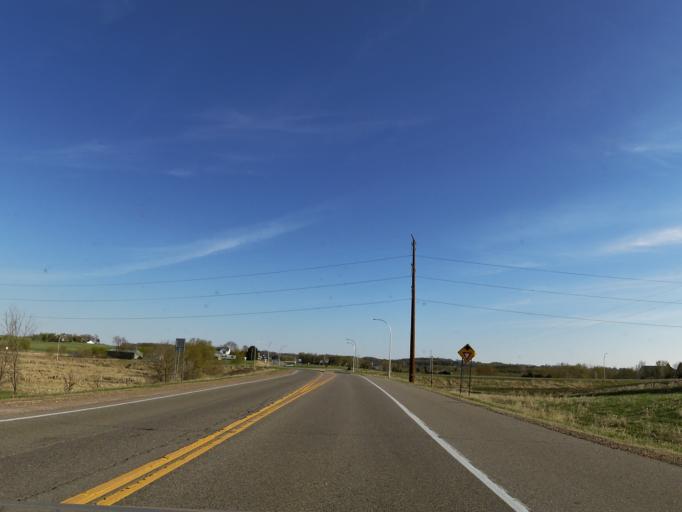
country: US
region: Minnesota
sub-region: Le Sueur County
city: New Prague
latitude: 44.5747
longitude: -93.5061
